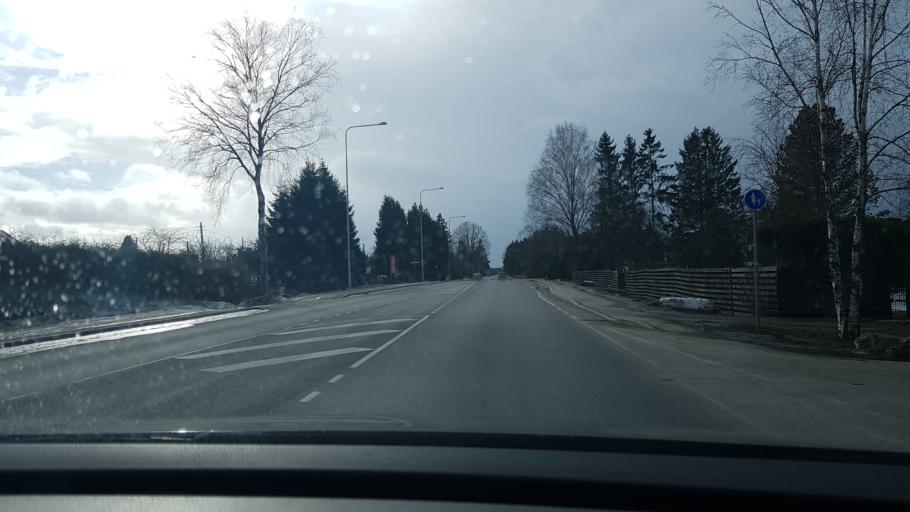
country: EE
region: Paernumaa
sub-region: Paikuse vald
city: Paikuse
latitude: 58.3839
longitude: 24.5967
